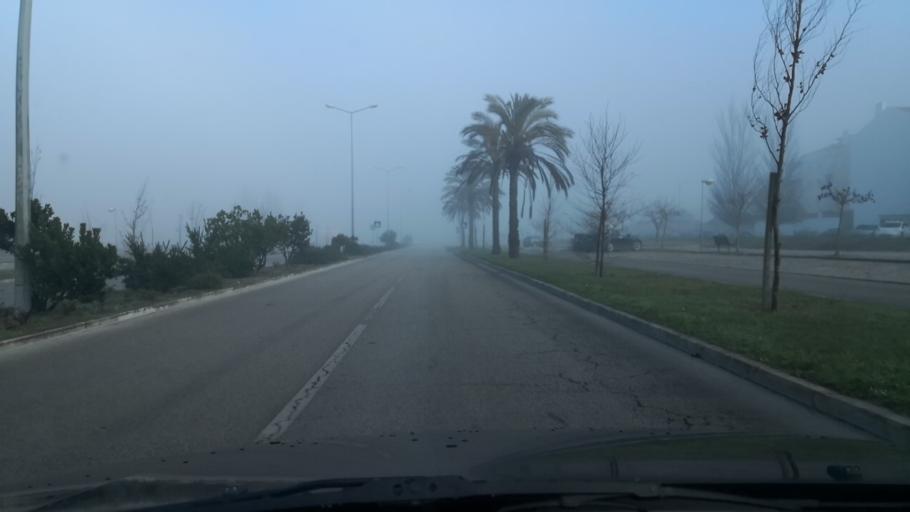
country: PT
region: Setubal
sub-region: Palmela
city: Pinhal Novo
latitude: 38.6254
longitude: -8.9181
